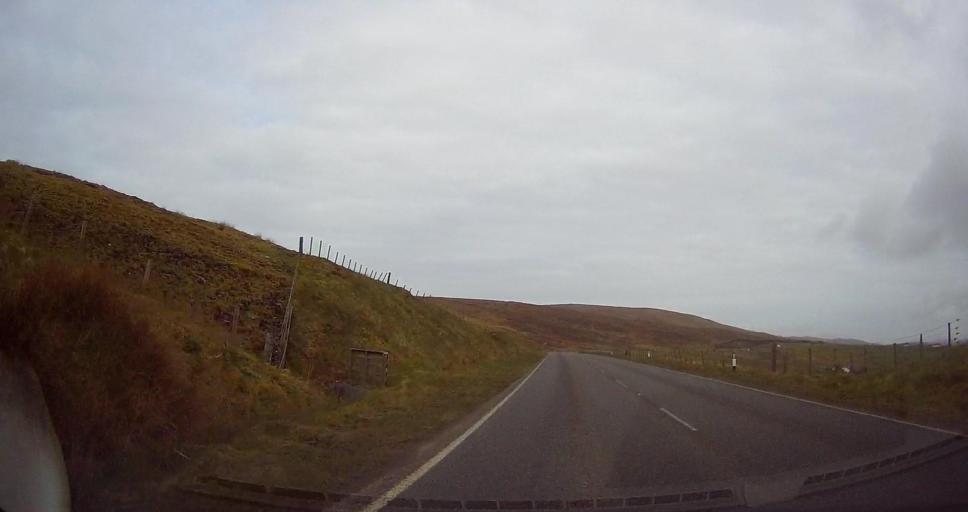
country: GB
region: Scotland
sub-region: Shetland Islands
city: Sandwick
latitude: 60.0687
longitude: -1.2261
